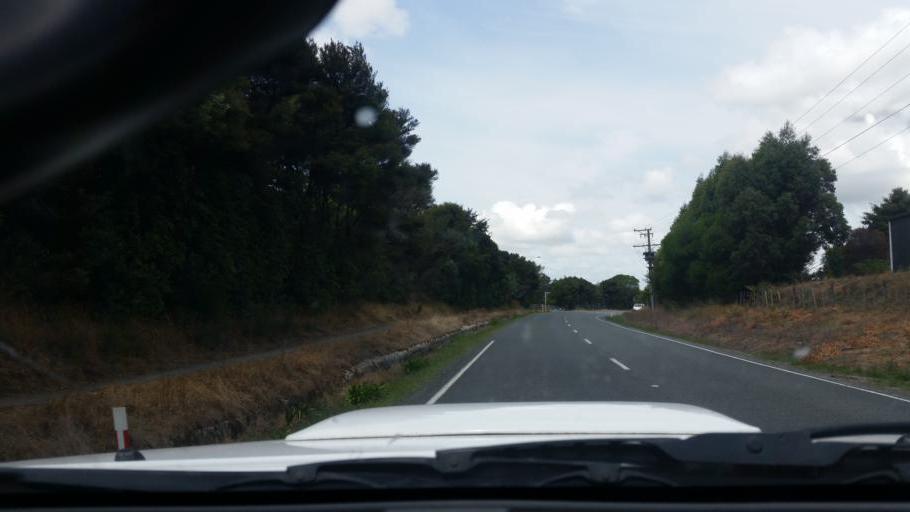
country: NZ
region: Auckland
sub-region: Auckland
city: Wellsford
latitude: -36.1142
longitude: 174.5751
